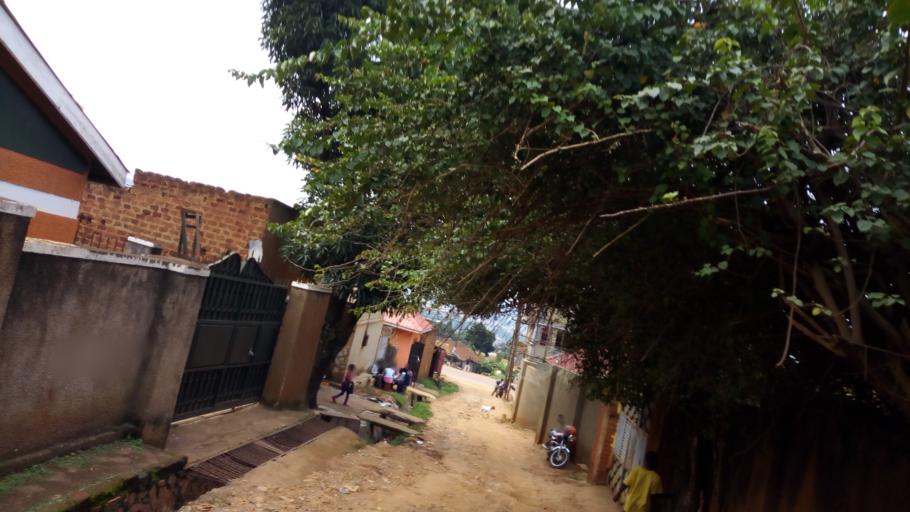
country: UG
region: Central Region
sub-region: Wakiso District
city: Kireka
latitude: 0.3205
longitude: 32.6444
